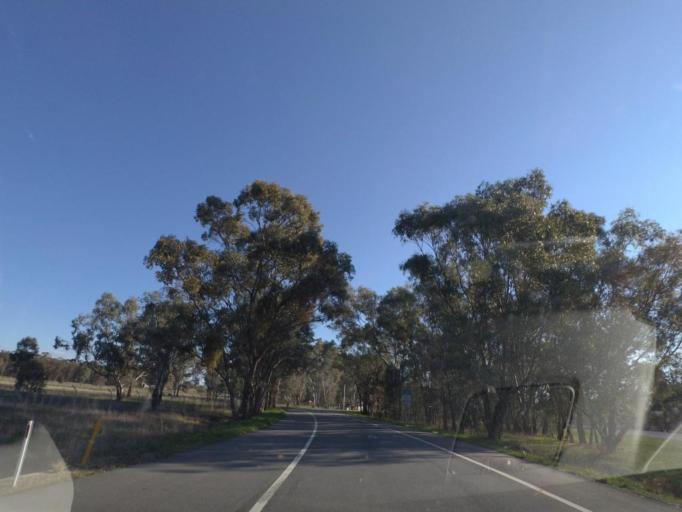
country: AU
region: Victoria
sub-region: Benalla
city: Benalla
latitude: -36.5769
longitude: 145.9226
